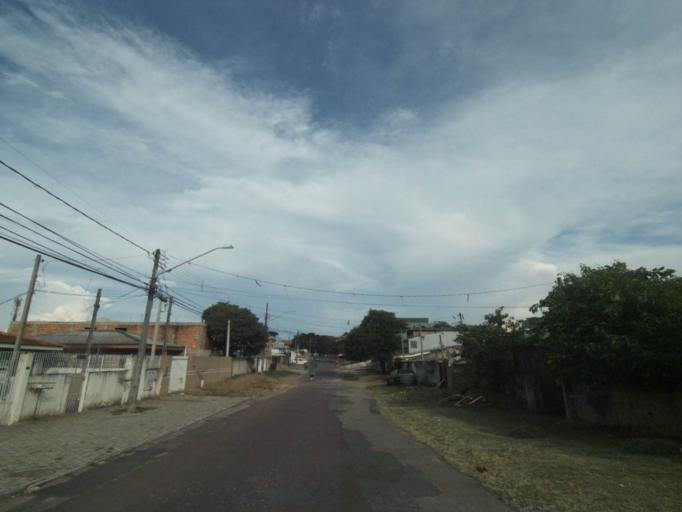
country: BR
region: Parana
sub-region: Pinhais
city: Pinhais
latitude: -25.4485
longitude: -49.2235
